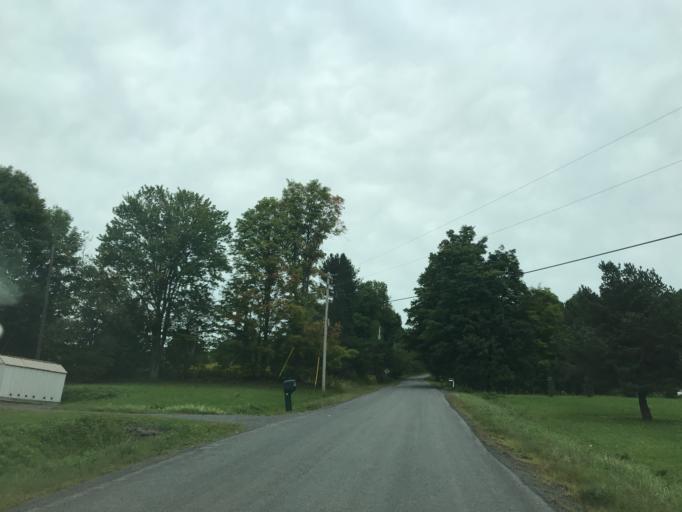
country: US
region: New York
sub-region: Otsego County
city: Worcester
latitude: 42.5399
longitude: -74.6590
